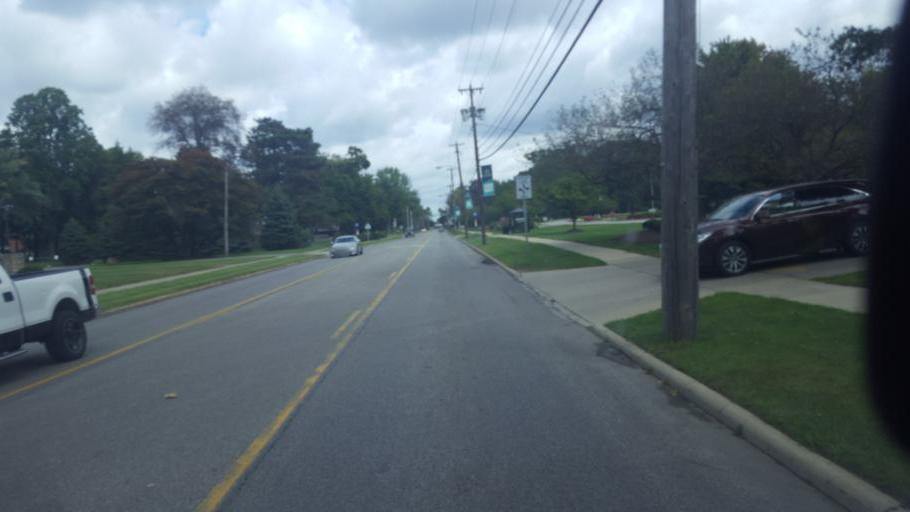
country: US
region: Ohio
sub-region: Lake County
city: Painesville
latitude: 41.7171
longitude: -81.2548
